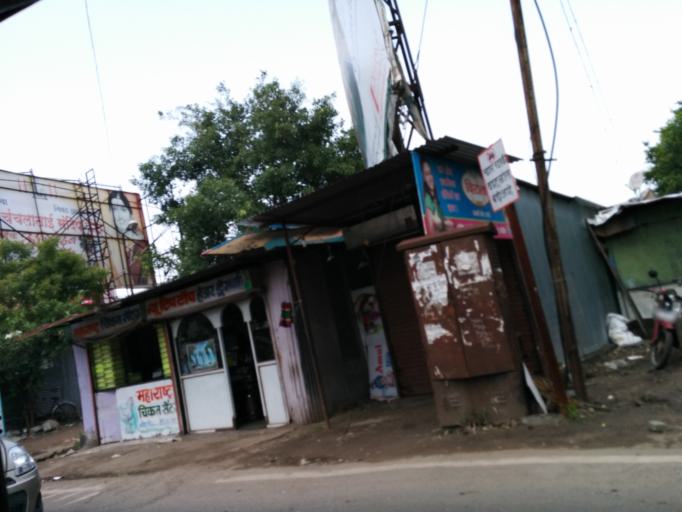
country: IN
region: Maharashtra
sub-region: Pune Division
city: Lohogaon
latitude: 18.5331
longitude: 73.9321
